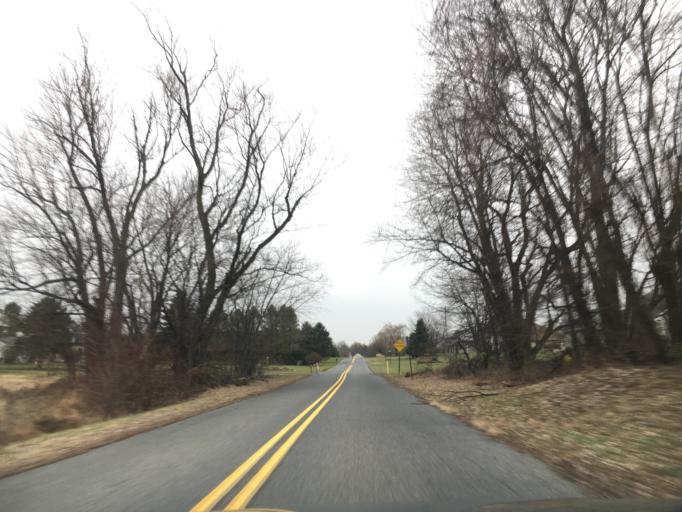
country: US
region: Pennsylvania
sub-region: Lehigh County
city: Schnecksville
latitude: 40.6890
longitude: -75.5835
